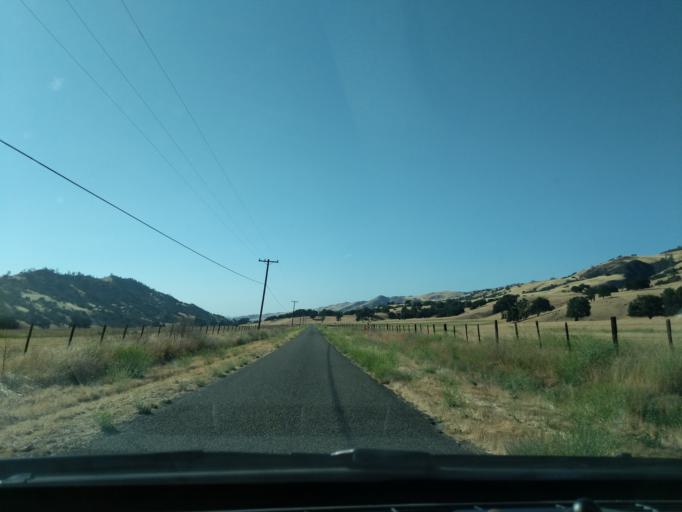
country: US
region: California
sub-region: San Luis Obispo County
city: San Miguel
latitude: 36.1216
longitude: -120.7342
